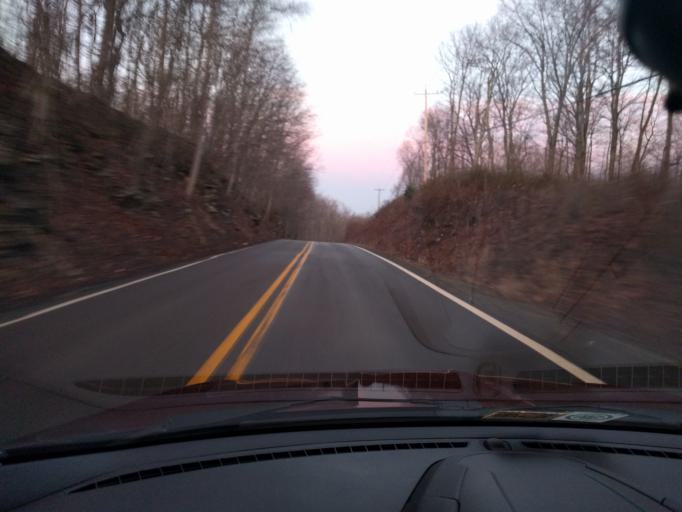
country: US
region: West Virginia
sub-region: Greenbrier County
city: Rainelle
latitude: 38.0157
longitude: -80.9042
